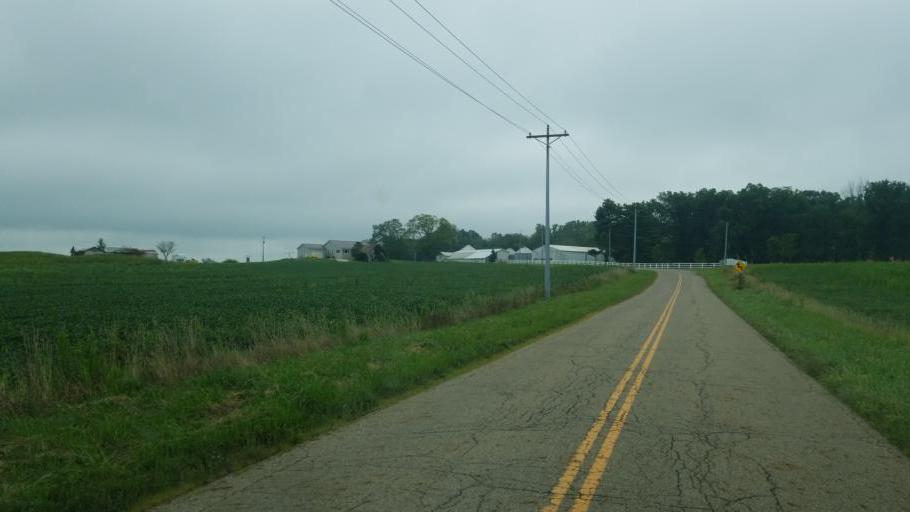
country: US
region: Ohio
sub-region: Licking County
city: Utica
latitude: 40.2892
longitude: -82.4299
